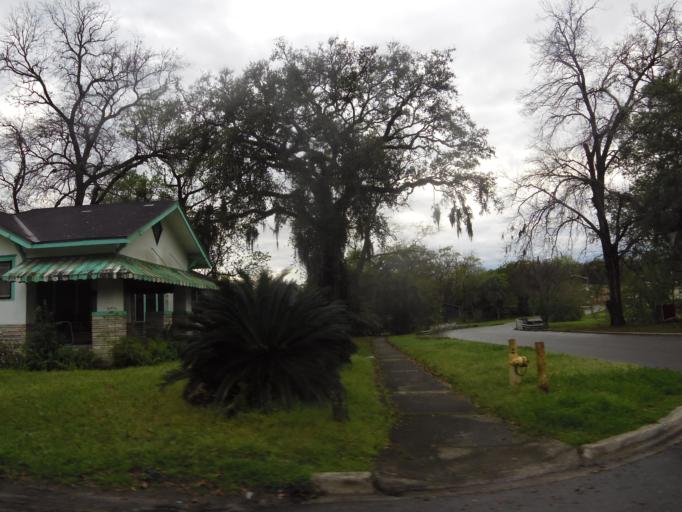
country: US
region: Florida
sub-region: Duval County
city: Jacksonville
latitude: 30.3253
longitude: -81.6997
